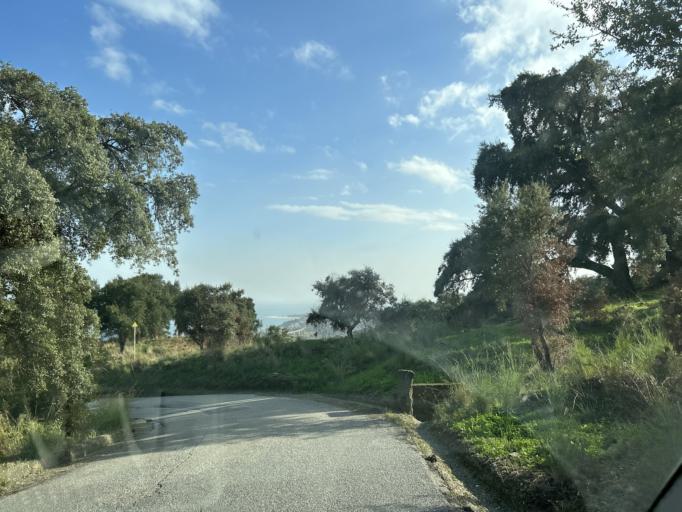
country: IT
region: Calabria
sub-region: Provincia di Catanzaro
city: Montepaone
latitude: 38.7184
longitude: 16.5095
